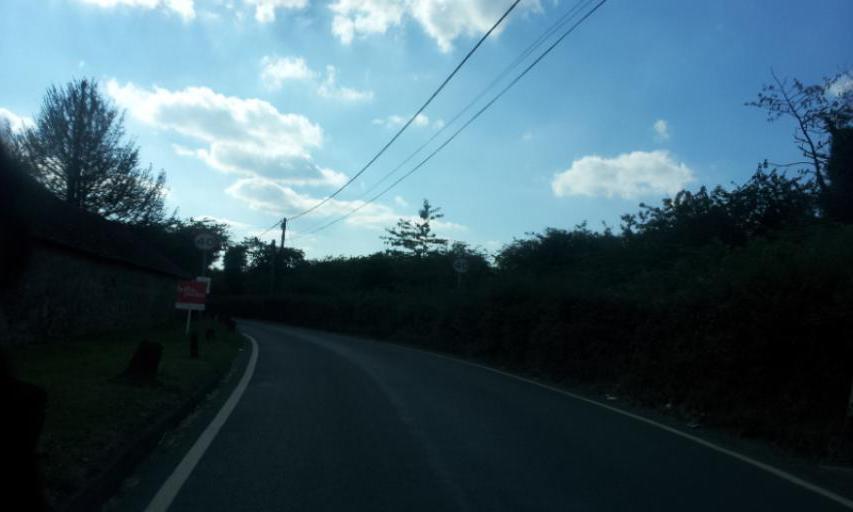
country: GB
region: England
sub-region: Kent
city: Headcorn
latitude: 51.2369
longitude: 0.5908
